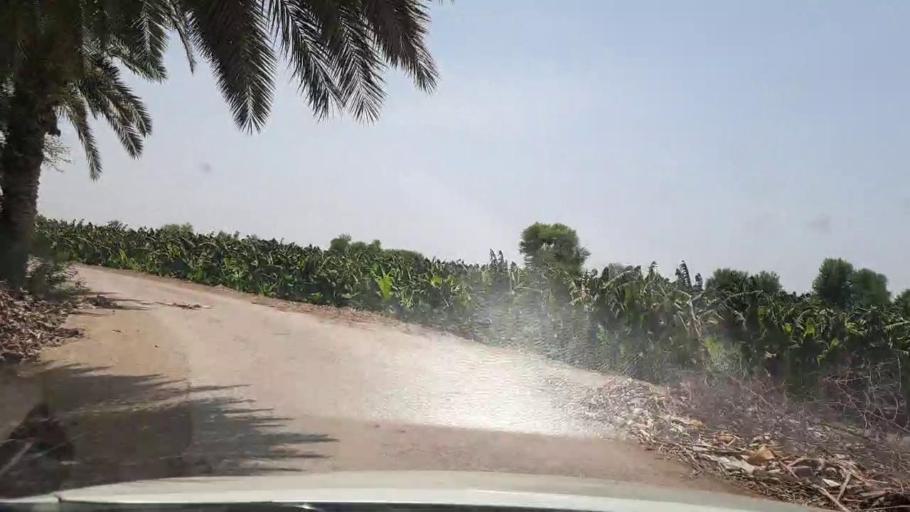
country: PK
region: Sindh
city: Bozdar
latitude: 27.2042
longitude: 68.6700
